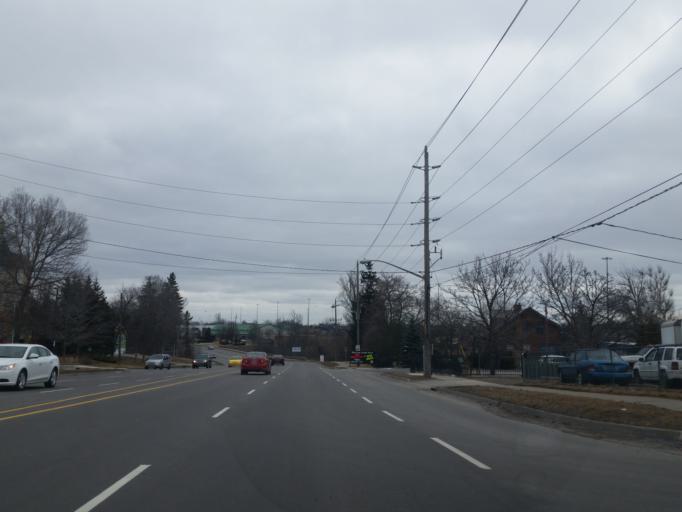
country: CA
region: Ontario
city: Pickering
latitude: 43.8099
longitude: -79.1282
